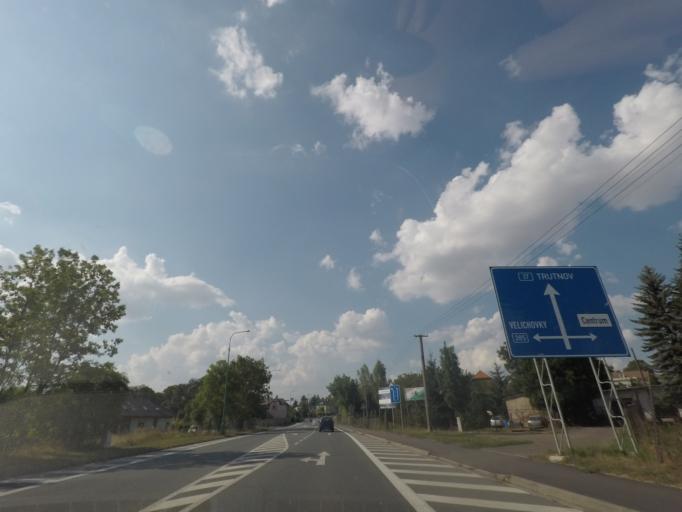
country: CZ
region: Kralovehradecky
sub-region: Okres Nachod
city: Jaromer
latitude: 50.3547
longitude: 15.9065
